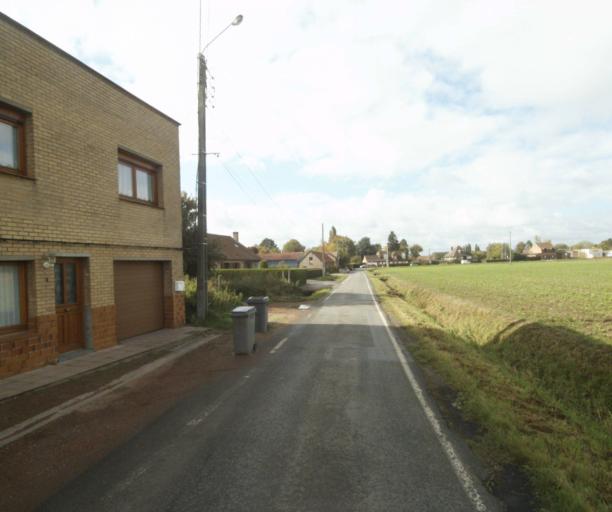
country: FR
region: Nord-Pas-de-Calais
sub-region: Departement du Nord
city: Verlinghem
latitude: 50.6791
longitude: 3.0136
